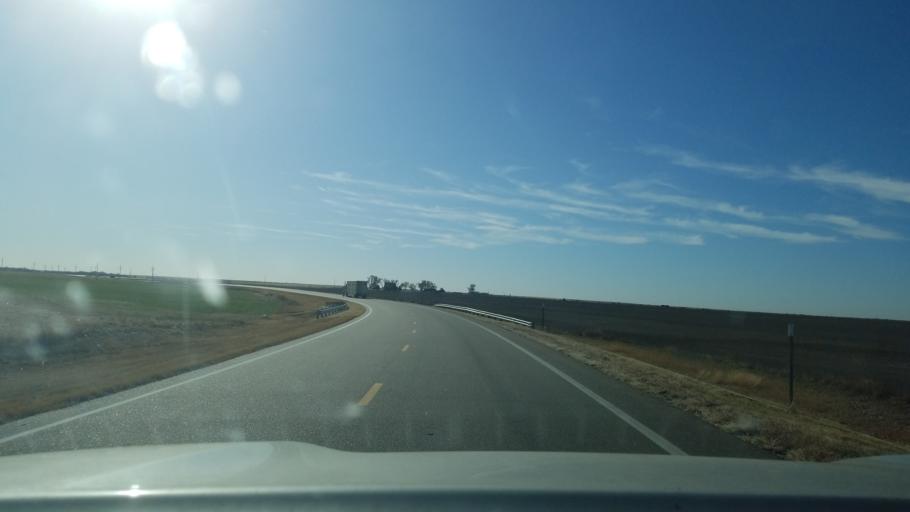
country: US
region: Kansas
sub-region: Ness County
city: Ness City
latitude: 38.4343
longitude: -99.9045
